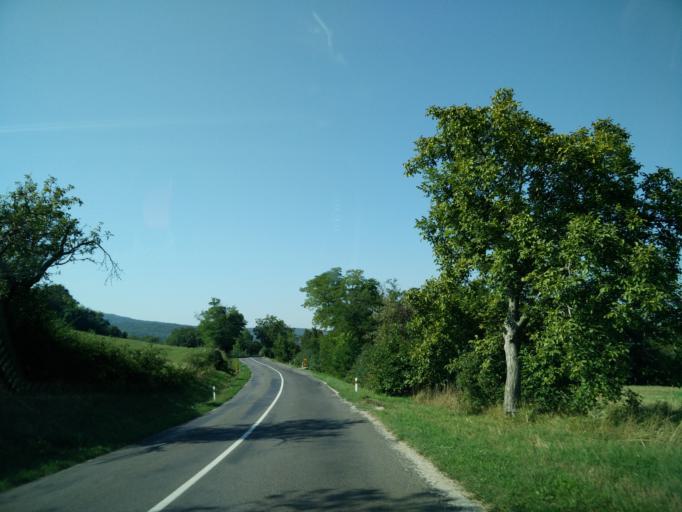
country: SK
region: Nitriansky
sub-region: Okres Nitra
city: Nitra
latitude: 48.3838
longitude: 18.0950
